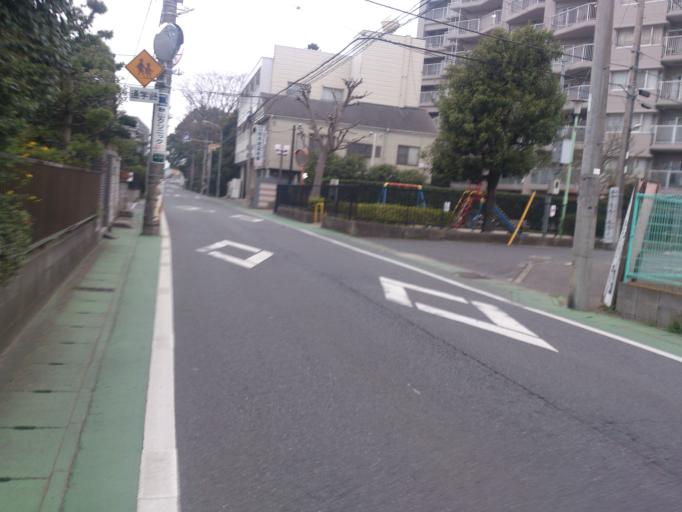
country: JP
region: Chiba
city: Kashiwa
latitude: 35.8037
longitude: 139.9574
